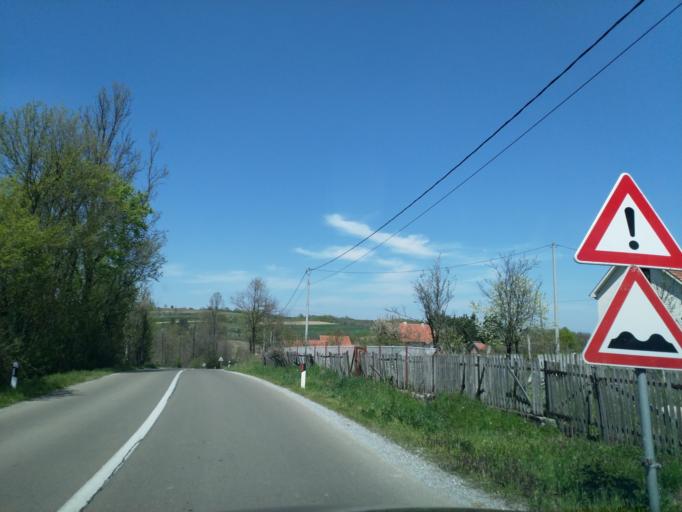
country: RS
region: Central Serbia
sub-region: Belgrade
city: Lazarevac
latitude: 44.3503
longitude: 20.3789
